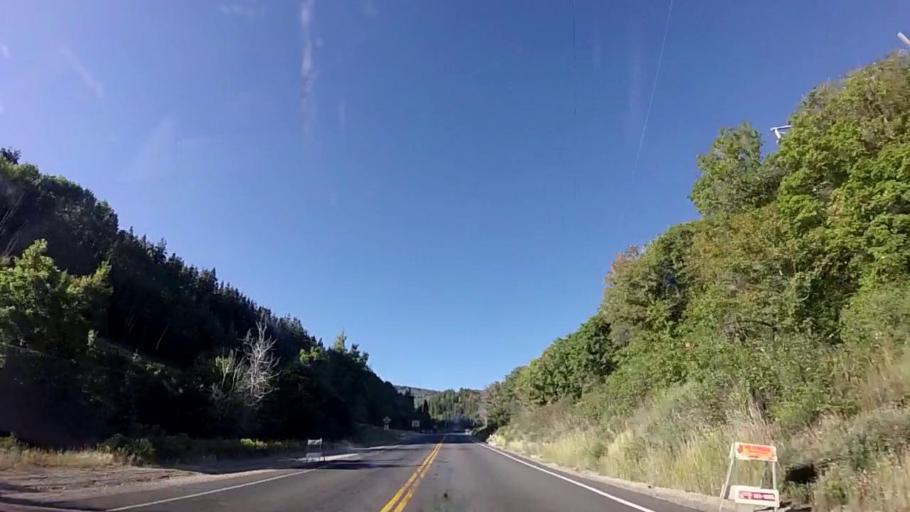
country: US
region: Utah
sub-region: Summit County
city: Park City
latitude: 40.6377
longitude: -111.4933
